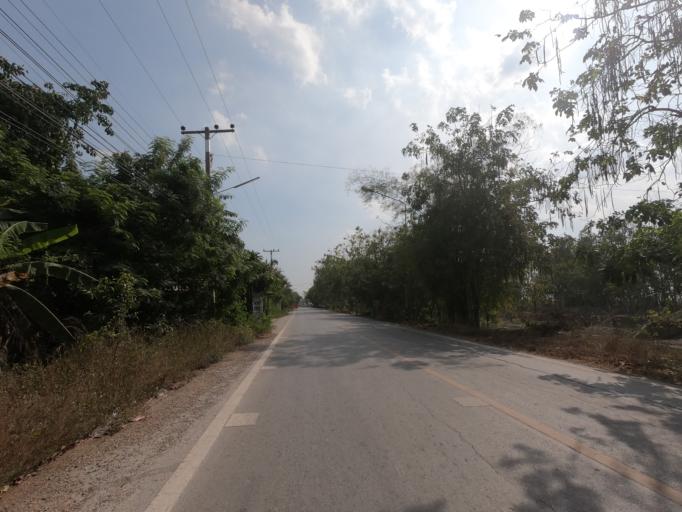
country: TH
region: Pathum Thani
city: Nong Suea
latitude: 14.1166
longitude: 100.8465
